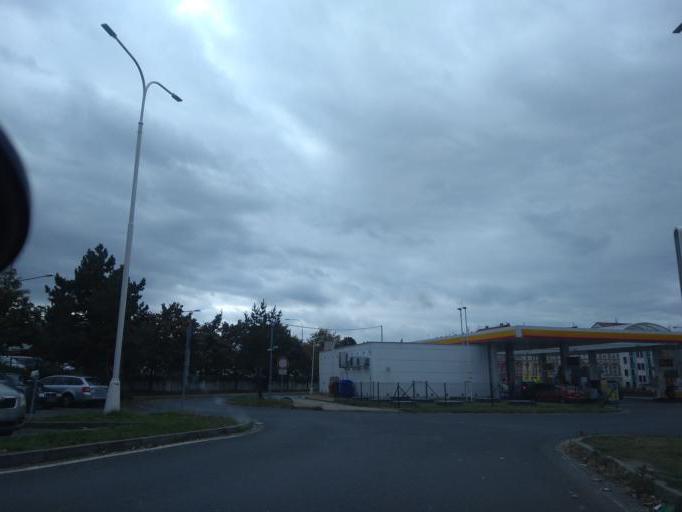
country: CZ
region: Plzensky
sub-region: Okres Plzen-Mesto
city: Pilsen
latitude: 49.7476
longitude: 13.3656
